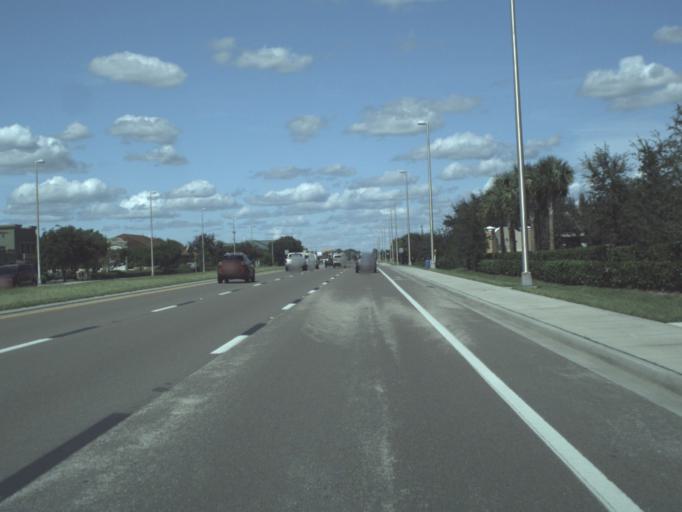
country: US
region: Florida
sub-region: Lee County
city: Villas
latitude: 26.5330
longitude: -81.8526
